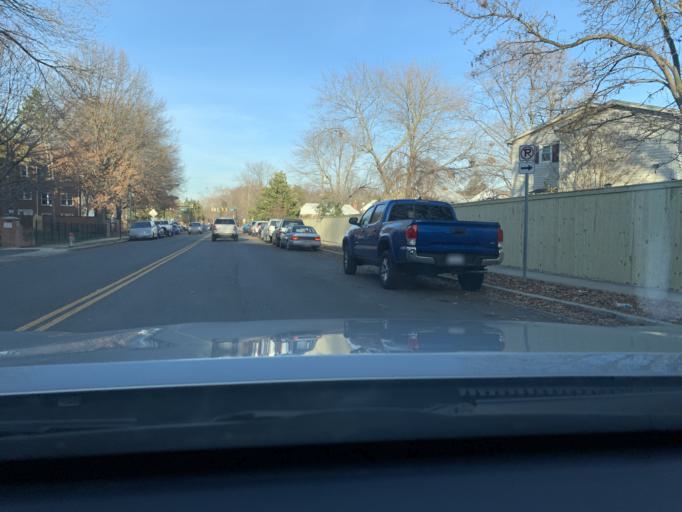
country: US
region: Virginia
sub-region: Fairfax County
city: Baileys Crossroads
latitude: 38.8648
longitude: -77.1352
